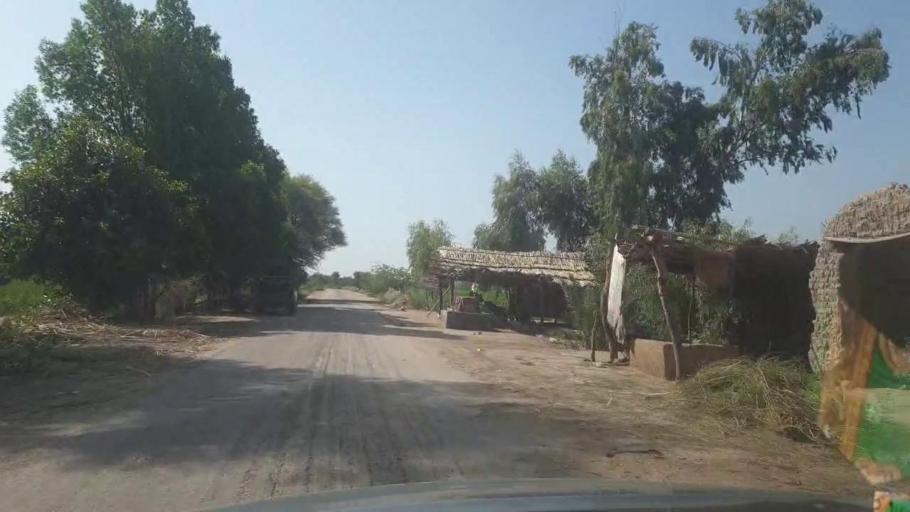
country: PK
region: Sindh
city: Rohri
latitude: 27.4679
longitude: 69.0371
